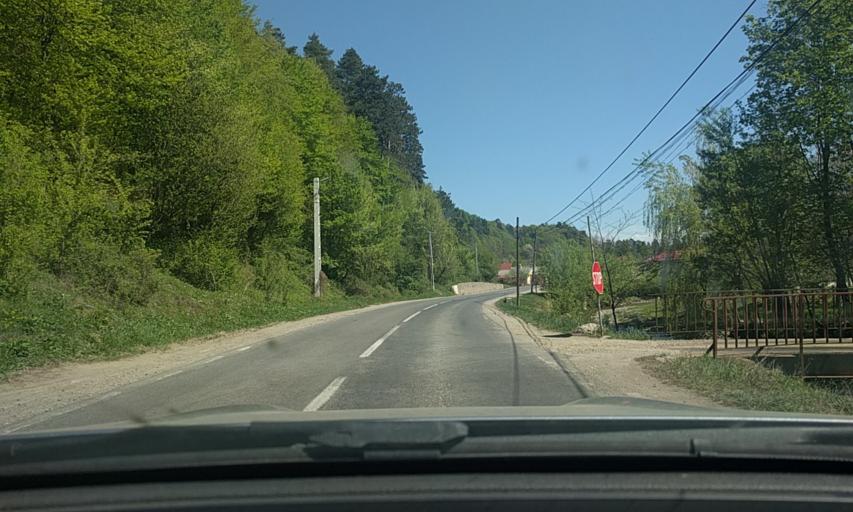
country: RO
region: Brasov
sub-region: Comuna Teliu
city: Teliu
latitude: 45.6947
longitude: 25.8698
